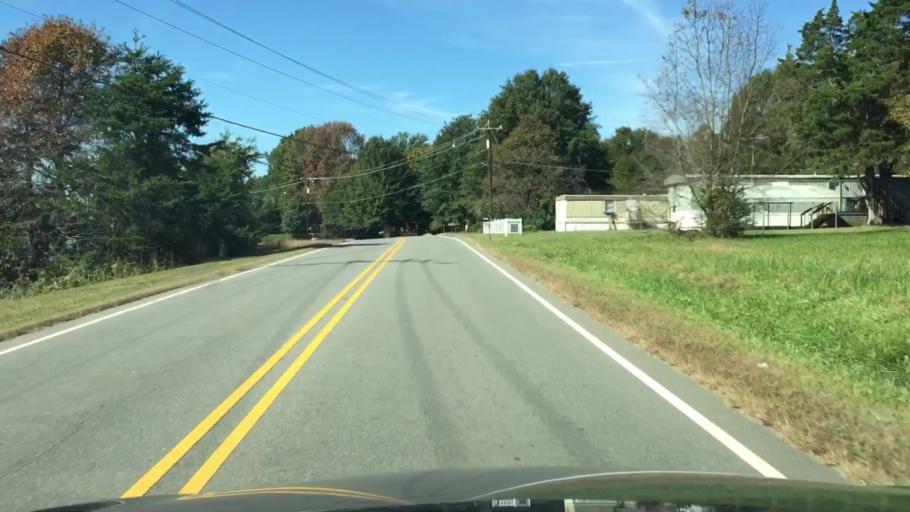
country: US
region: North Carolina
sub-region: Rockingham County
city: Reidsville
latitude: 36.3279
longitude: -79.6300
